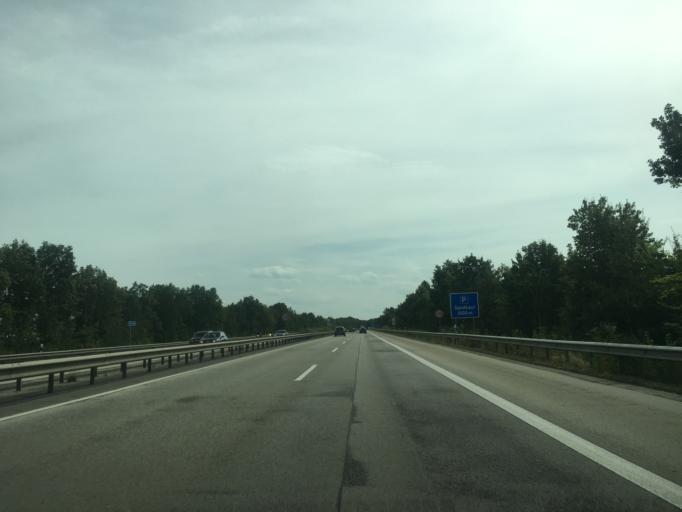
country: DE
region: Rheinland-Pfalz
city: Winningen
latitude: 50.3457
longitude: 7.5023
